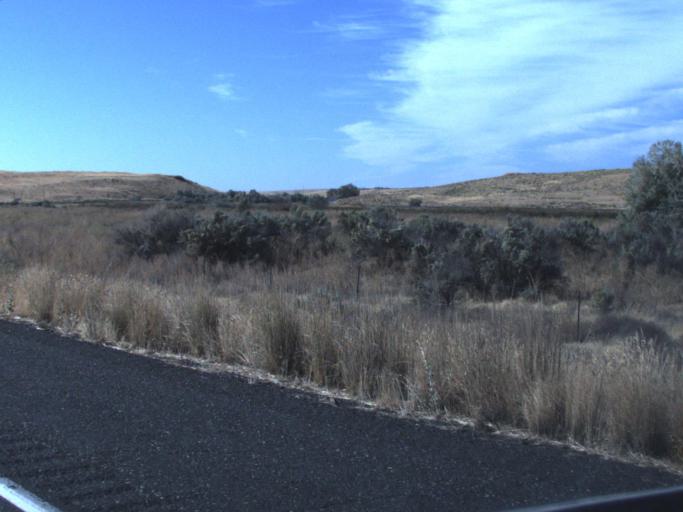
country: US
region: Washington
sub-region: Franklin County
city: Basin City
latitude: 46.4346
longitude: -119.0237
